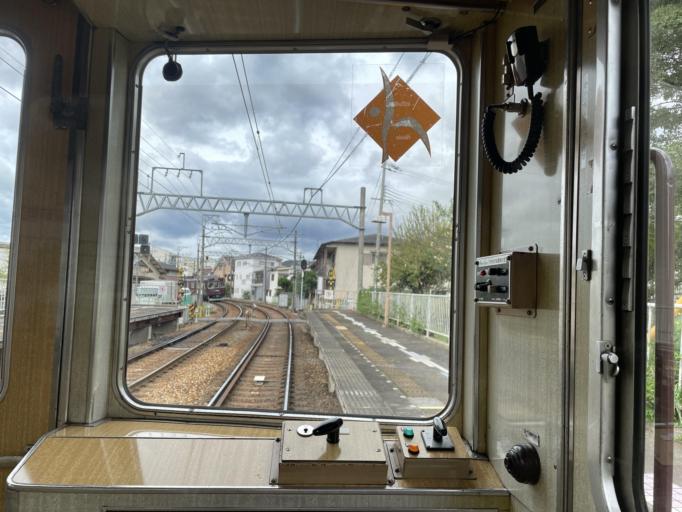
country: JP
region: Osaka
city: Ikeda
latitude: 34.8351
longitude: 135.4232
